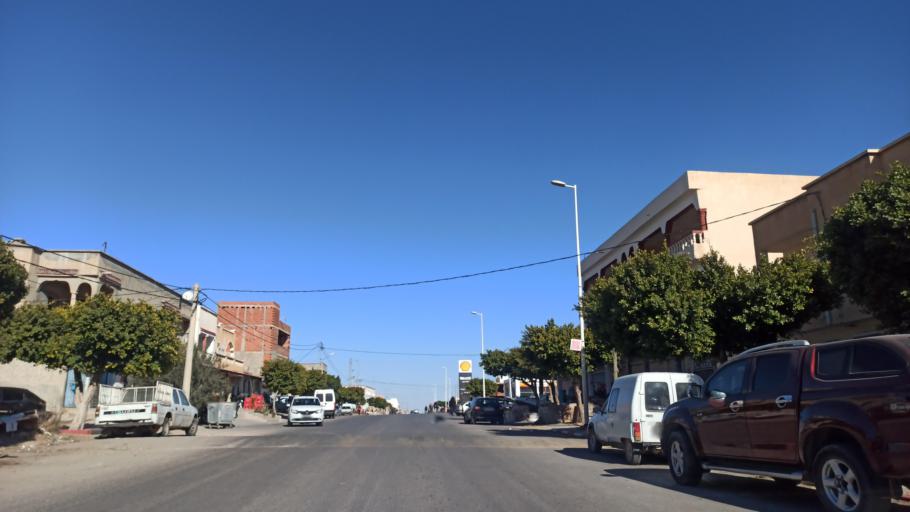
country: TN
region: Sidi Bu Zayd
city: Bi'r al Hufayy
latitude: 34.9381
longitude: 9.2009
